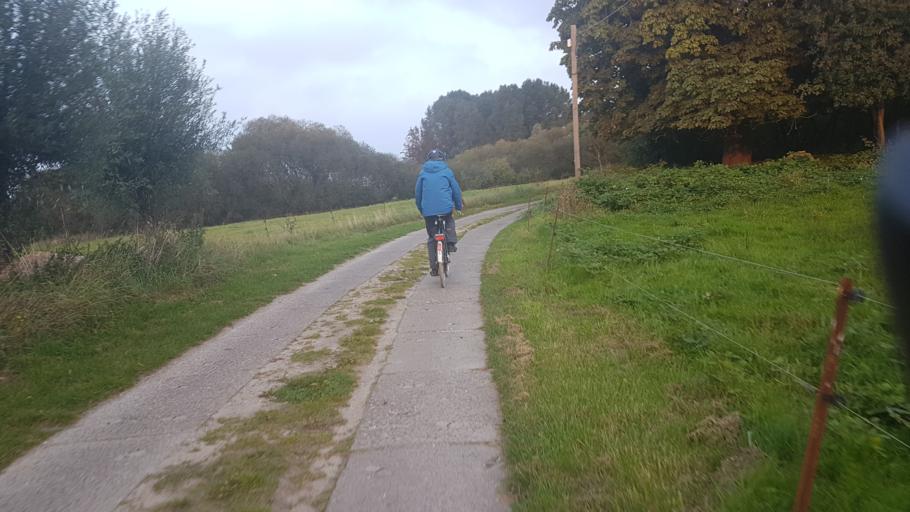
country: DE
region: Mecklenburg-Vorpommern
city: Putbus
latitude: 54.3490
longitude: 13.5349
